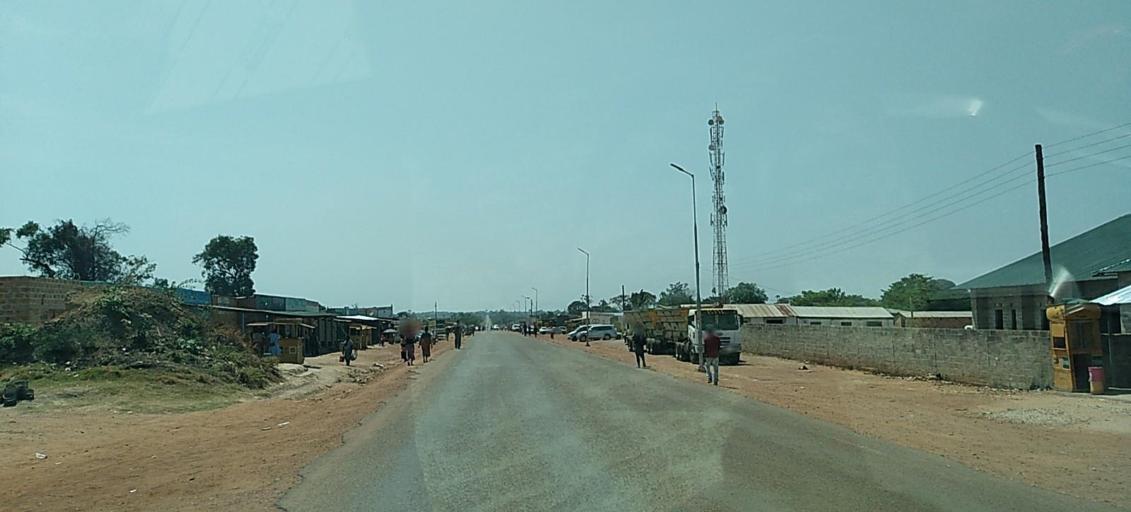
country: ZM
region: North-Western
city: Solwezi
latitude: -12.3126
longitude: 25.8479
